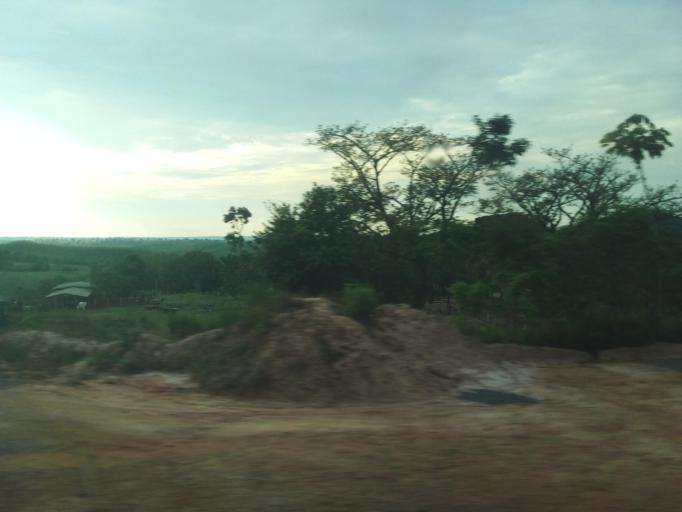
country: BR
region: Maranhao
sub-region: Imperatriz
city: Imperatriz
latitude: -4.7874
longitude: -47.2995
